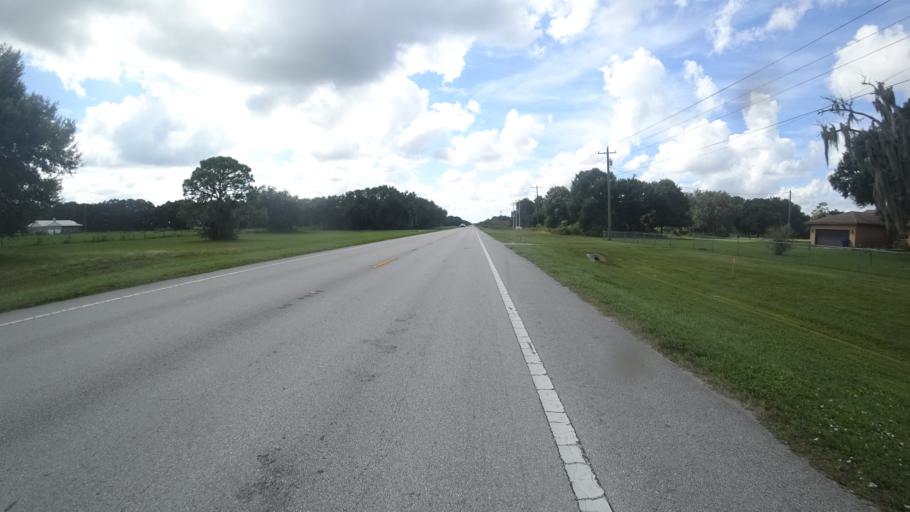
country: US
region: Florida
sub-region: Hillsborough County
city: Ruskin
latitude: 27.6235
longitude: -82.4054
